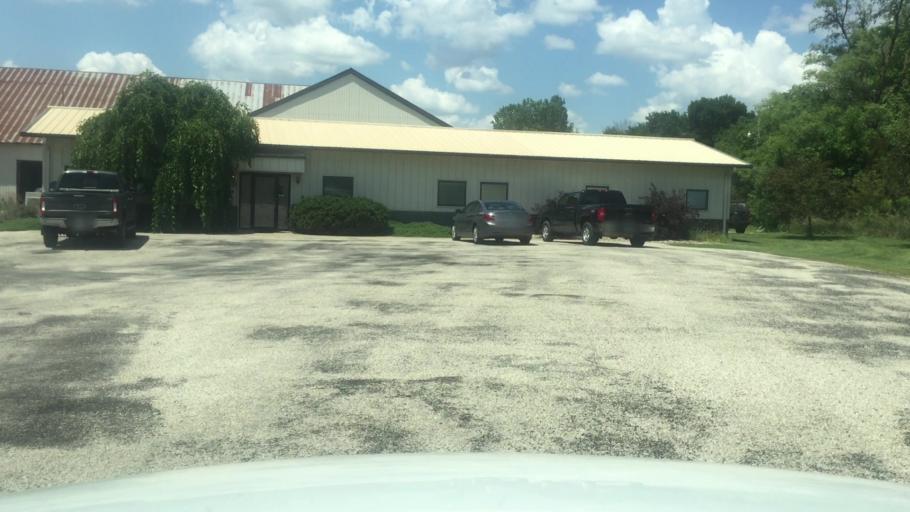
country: US
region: Kansas
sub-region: Brown County
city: Horton
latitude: 39.6571
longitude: -95.5290
